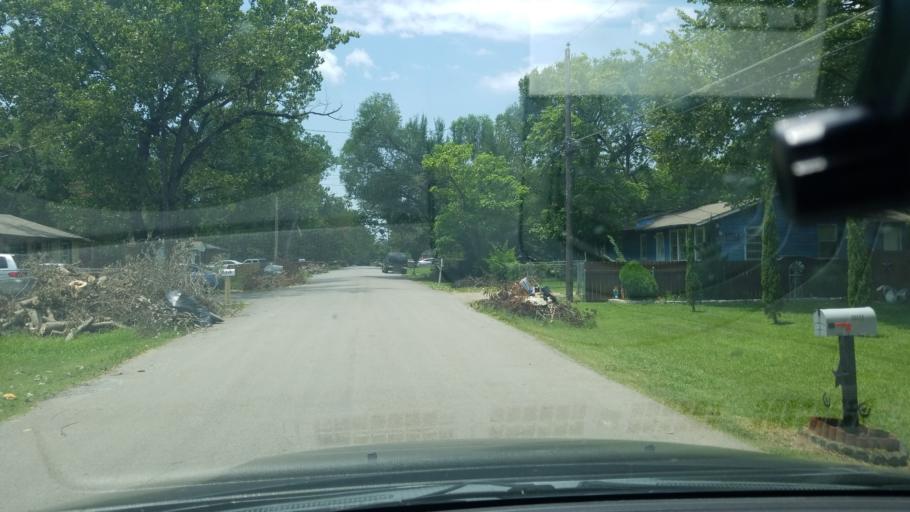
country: US
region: Texas
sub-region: Dallas County
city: Balch Springs
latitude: 32.7159
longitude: -96.6495
